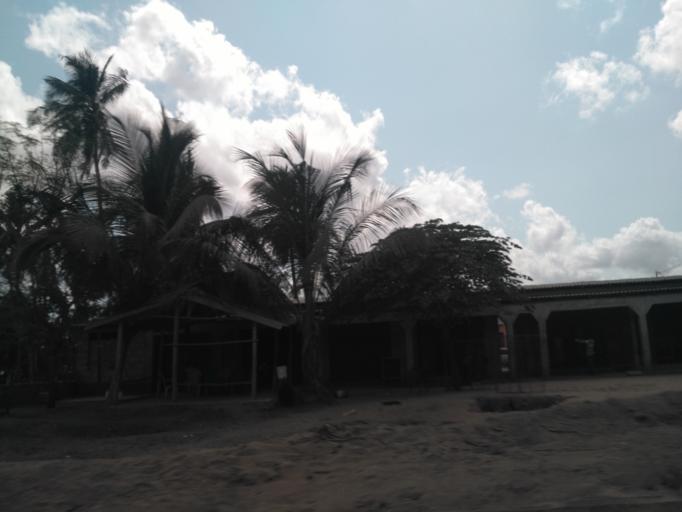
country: TZ
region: Dar es Salaam
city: Dar es Salaam
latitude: -6.8807
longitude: 39.3371
